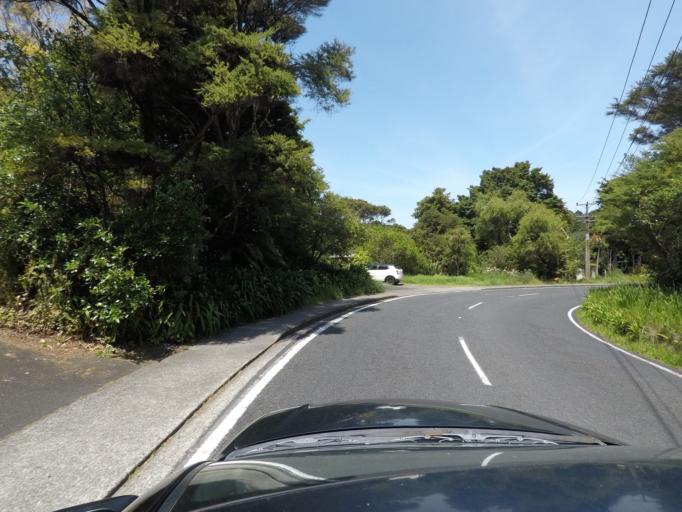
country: NZ
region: Auckland
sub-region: Auckland
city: Titirangi
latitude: -36.9634
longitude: 174.6416
